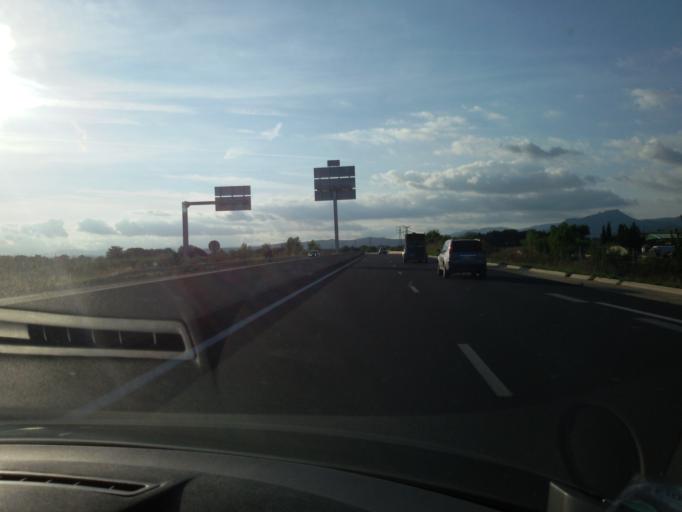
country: FR
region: Languedoc-Roussillon
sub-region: Departement de l'Herault
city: Saint-Andre-de-Sangonis
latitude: 43.6564
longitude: 3.5199
